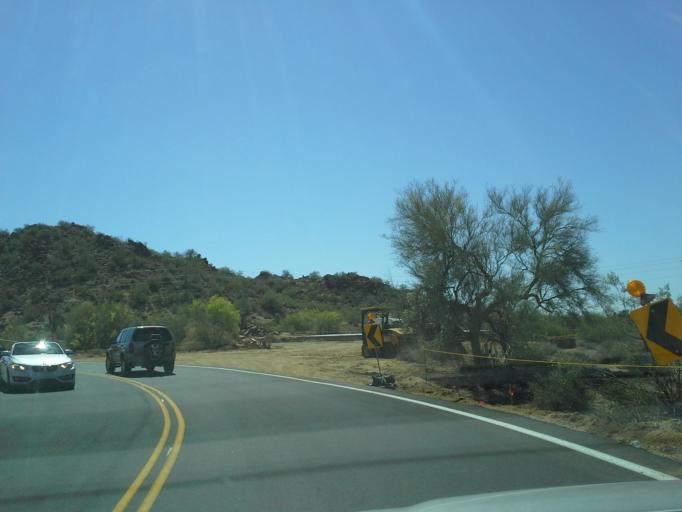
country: US
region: Arizona
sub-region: Pinal County
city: Apache Junction
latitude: 33.4513
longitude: -111.6356
